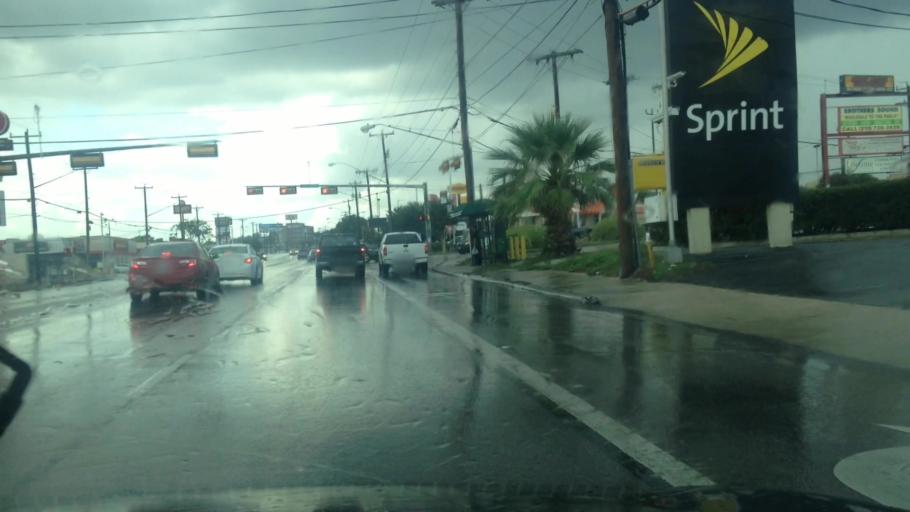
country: US
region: Texas
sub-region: Bexar County
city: Balcones Heights
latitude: 29.4889
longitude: -98.5501
